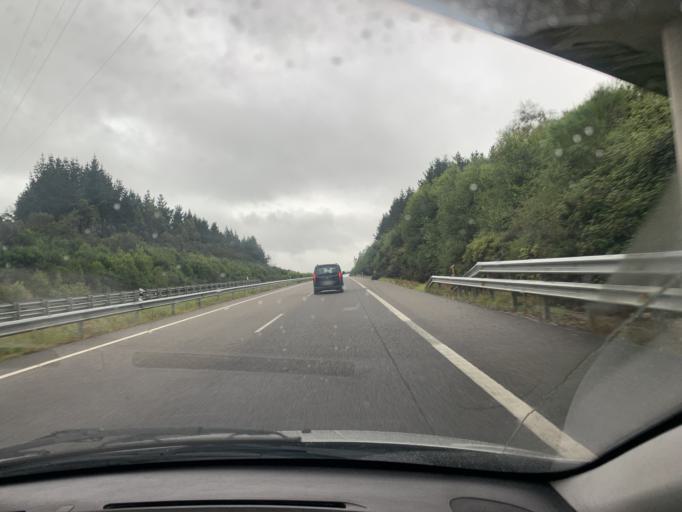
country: ES
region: Galicia
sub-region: Provincia de Lugo
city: Abadin
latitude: 43.3468
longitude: -7.5120
